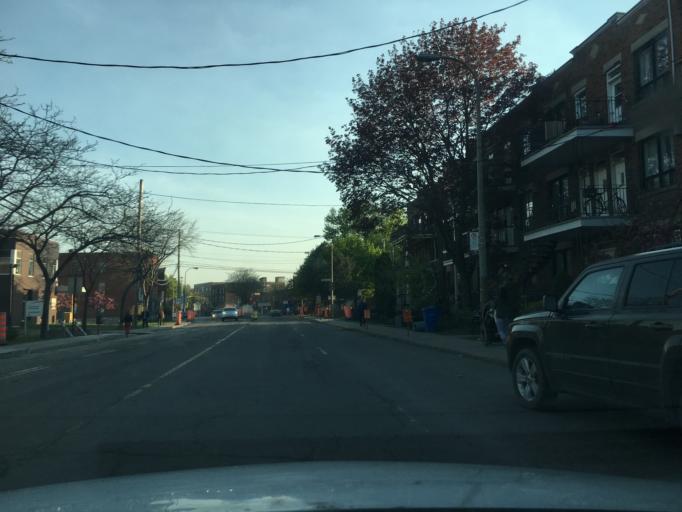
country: CA
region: Quebec
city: Westmount
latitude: 45.4690
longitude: -73.5655
